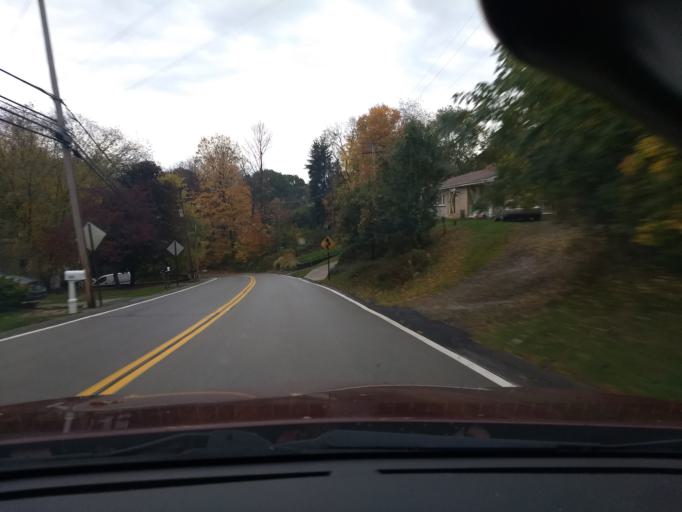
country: US
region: Pennsylvania
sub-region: Allegheny County
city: Jefferson Hills
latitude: 40.2966
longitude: -79.9261
